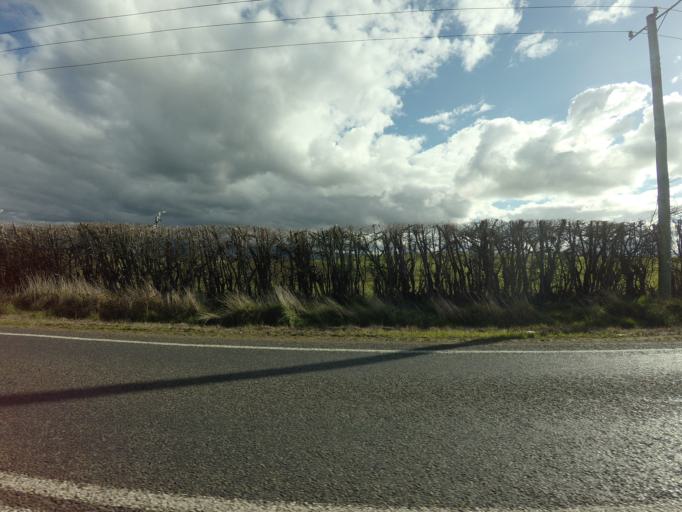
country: AU
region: Tasmania
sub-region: Northern Midlands
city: Longford
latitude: -41.7040
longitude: 147.0777
